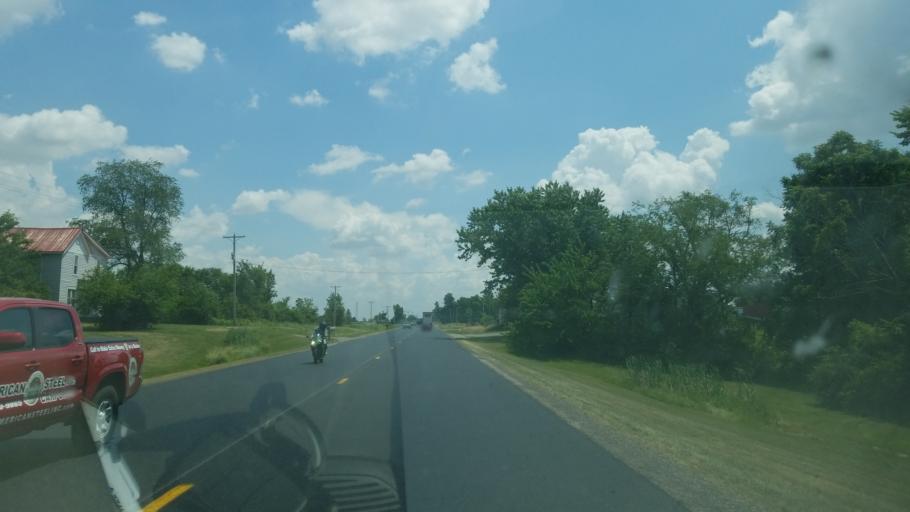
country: US
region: Ohio
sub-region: Allen County
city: Lima
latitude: 40.7315
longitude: -83.9648
